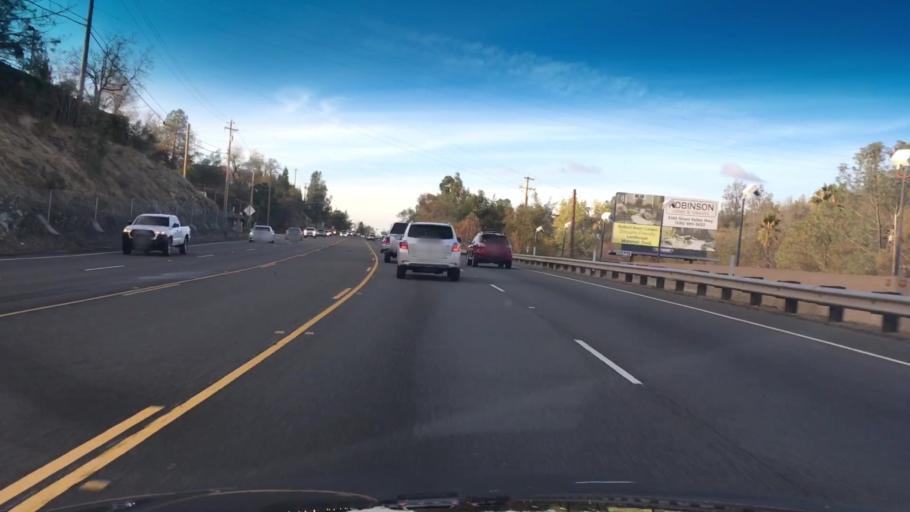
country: US
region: California
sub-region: Placer County
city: North Auburn
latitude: 38.9142
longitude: -121.0781
